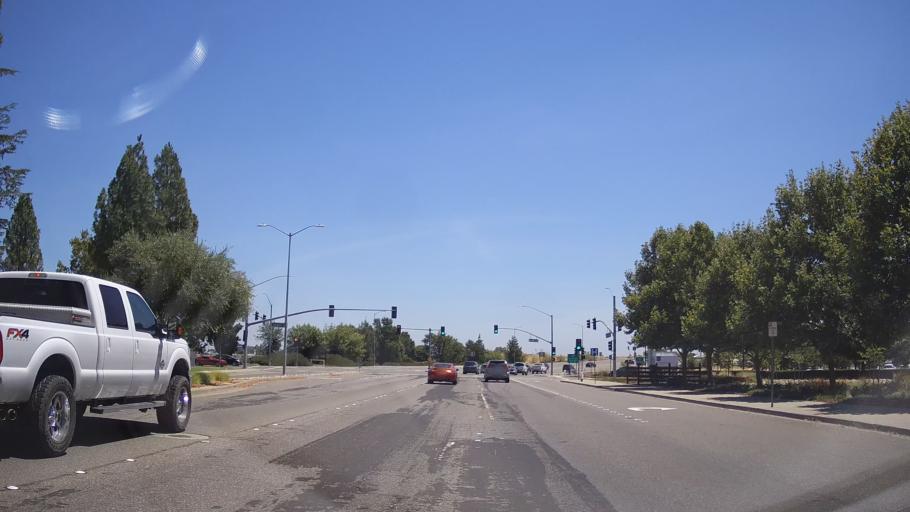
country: US
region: California
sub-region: Solano County
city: Hartley
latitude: 38.3901
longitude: -121.9381
